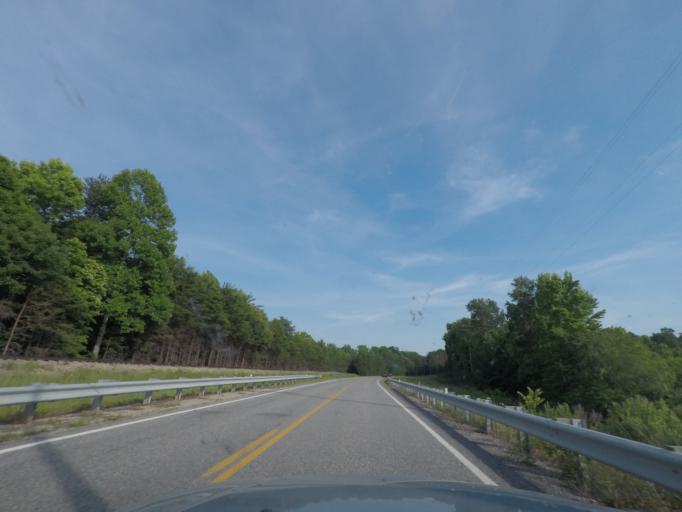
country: US
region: Virginia
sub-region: Mecklenburg County
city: Clarksville
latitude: 36.5675
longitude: -78.5444
